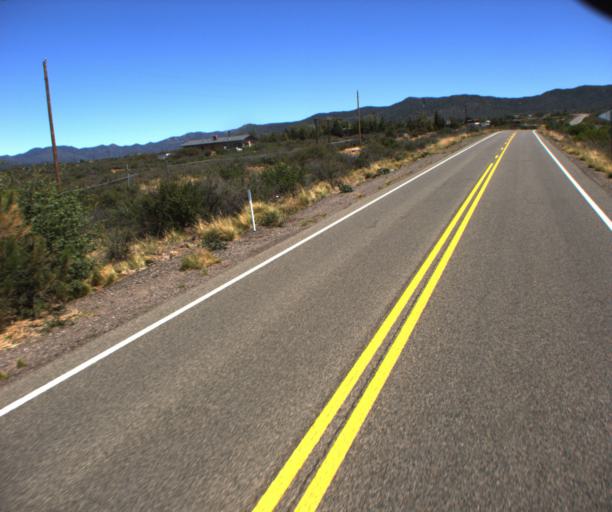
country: US
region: Arizona
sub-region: Yavapai County
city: Prescott
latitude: 34.4151
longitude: -112.6026
